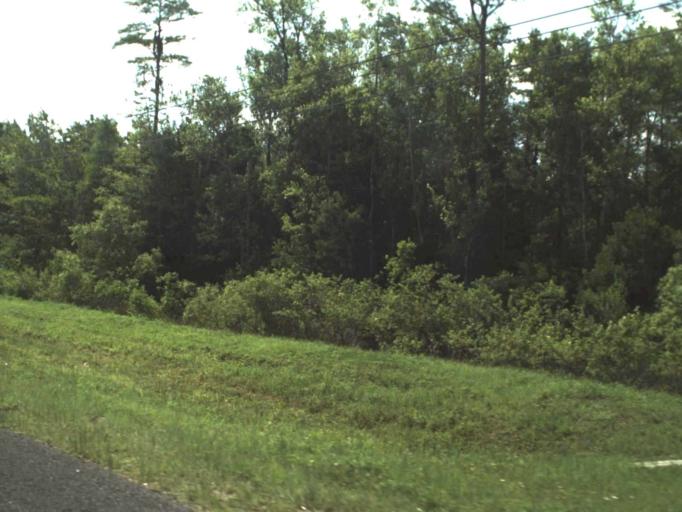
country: US
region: Florida
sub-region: Volusia County
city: Samsula-Spruce Creek
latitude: 29.0260
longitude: -81.1454
